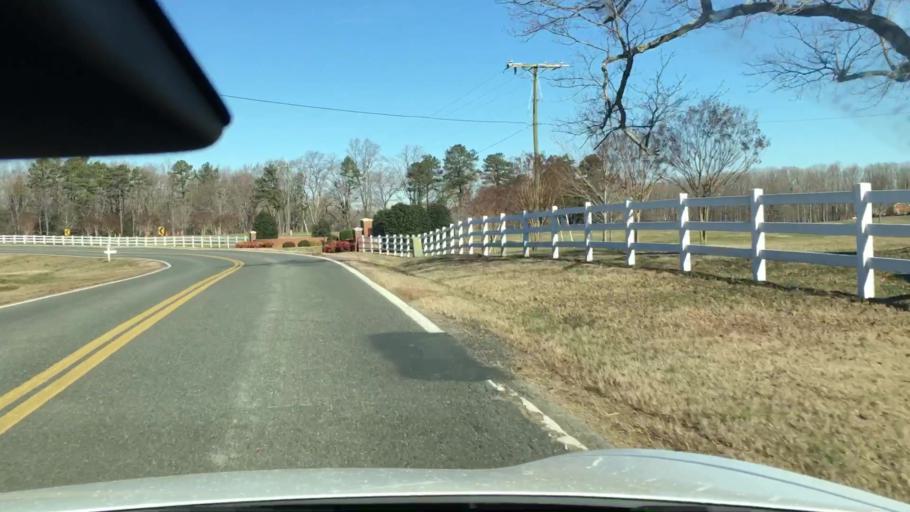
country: US
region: Virginia
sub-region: Powhatan County
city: Powhatan
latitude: 37.5494
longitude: -77.7925
